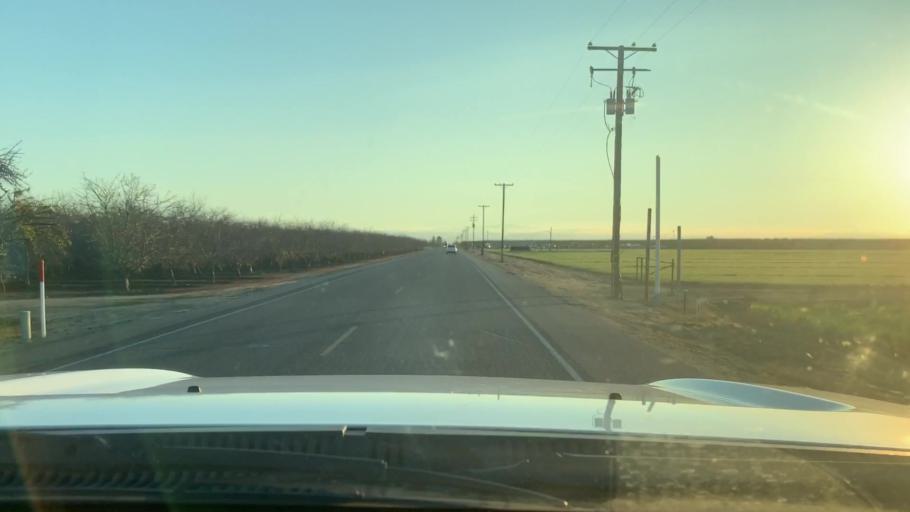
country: US
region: California
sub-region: Kern County
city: Shafter
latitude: 35.5001
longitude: -119.3548
